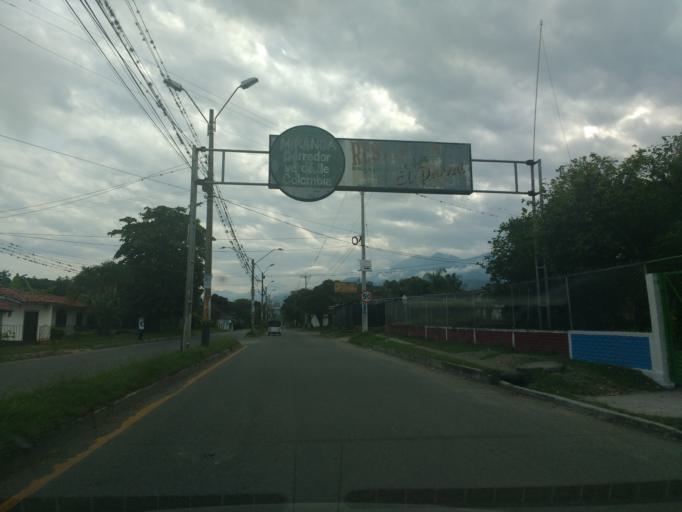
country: CO
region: Cauca
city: Miranda
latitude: 3.2683
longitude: -76.2247
